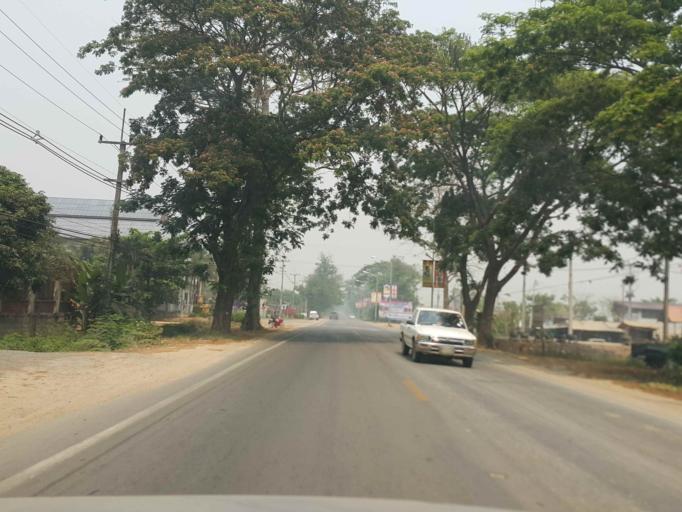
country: TH
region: Chiang Mai
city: Mae Taeng
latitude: 19.0134
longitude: 98.9711
